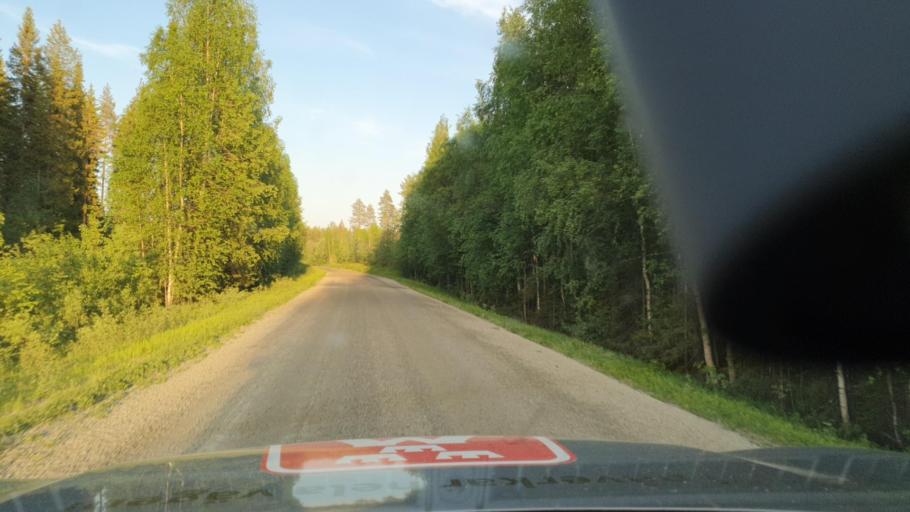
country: SE
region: Norrbotten
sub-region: Bodens Kommun
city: Boden
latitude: 66.1640
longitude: 21.5414
